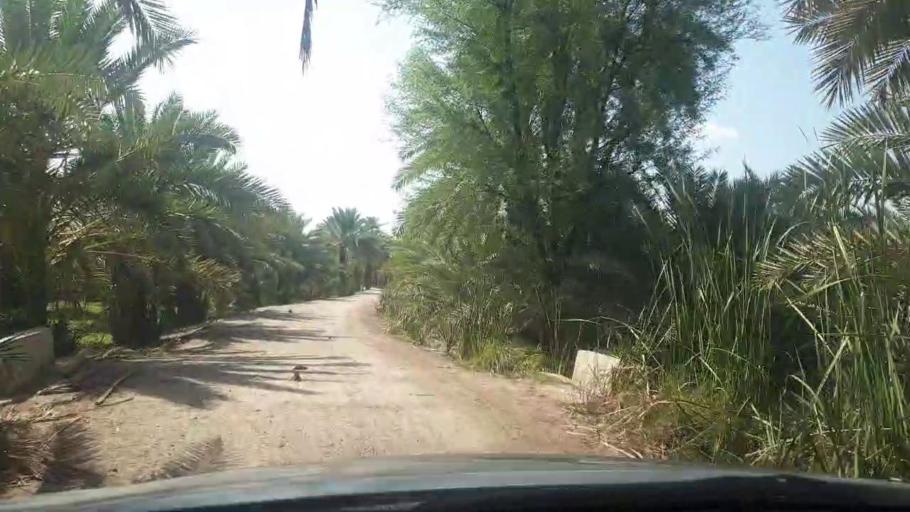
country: PK
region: Sindh
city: Khairpur
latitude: 27.5539
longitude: 68.8043
